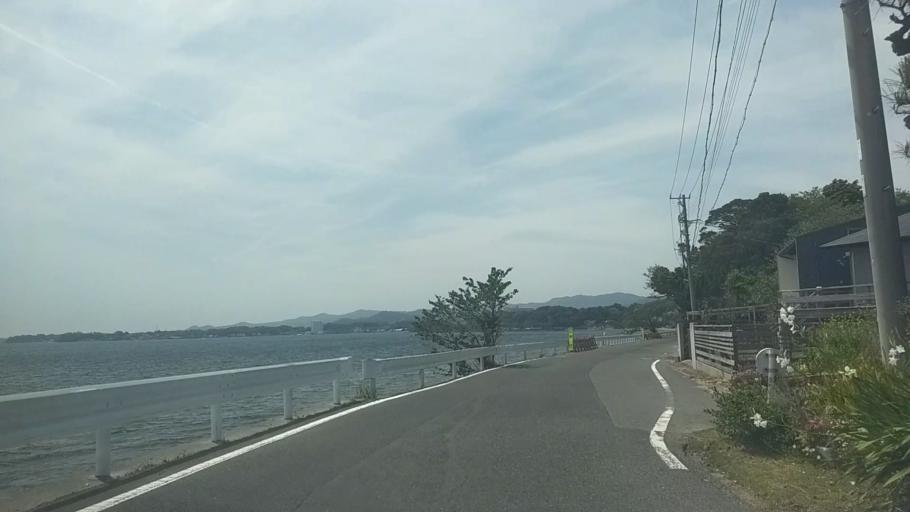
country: JP
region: Shizuoka
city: Kosai-shi
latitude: 34.7843
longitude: 137.5939
